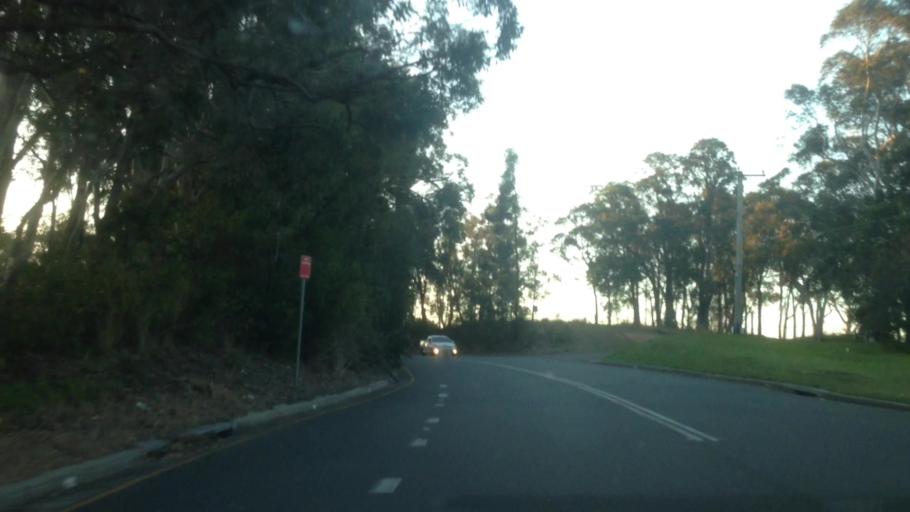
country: AU
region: New South Wales
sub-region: Wyong Shire
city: Kingfisher Shores
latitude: -33.1529
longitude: 151.5250
